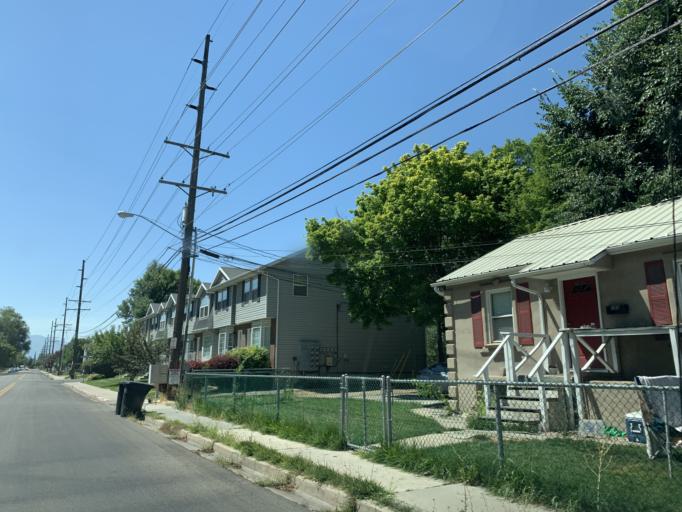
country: US
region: Utah
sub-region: Utah County
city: Provo
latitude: 40.2391
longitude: -111.6466
